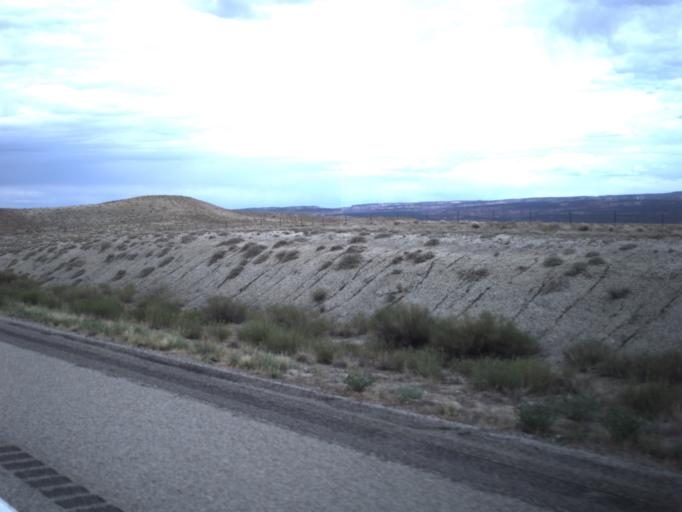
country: US
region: Utah
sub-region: Grand County
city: Moab
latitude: 38.9941
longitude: -109.3291
